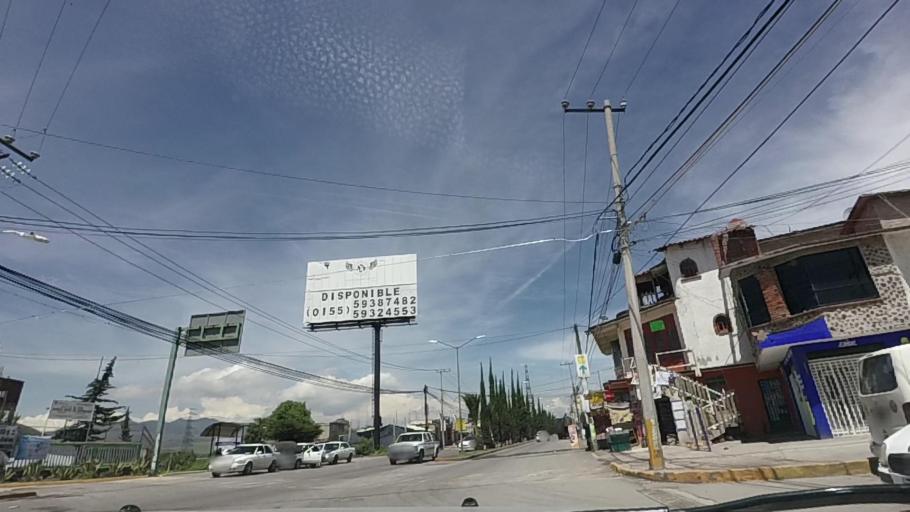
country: MX
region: Mexico
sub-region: Huehuetoca
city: Colonia Santa Teresa
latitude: 19.8305
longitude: -99.2263
